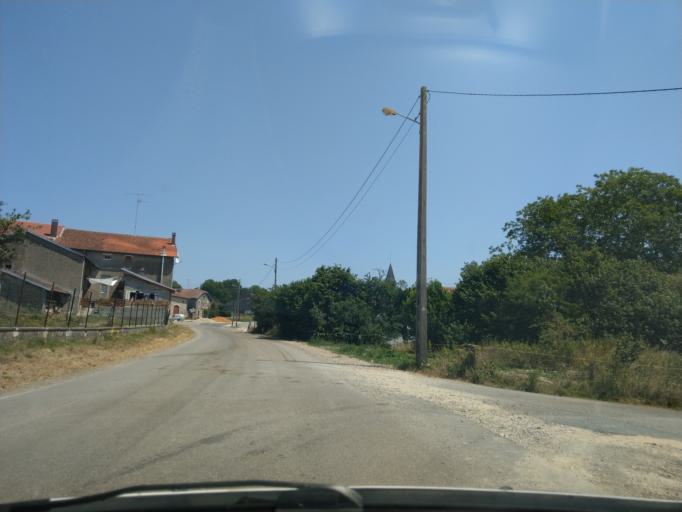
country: FR
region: Lorraine
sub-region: Departement de Meurthe-et-Moselle
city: Baccarat
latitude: 48.6267
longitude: 6.7852
